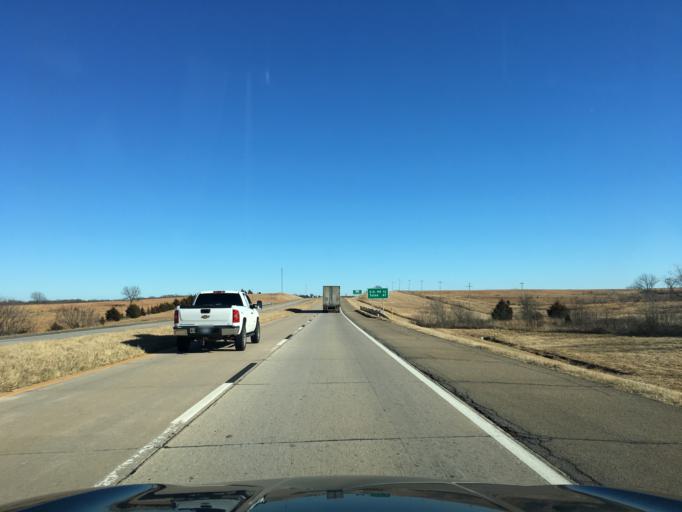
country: US
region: Oklahoma
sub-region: Pawnee County
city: Pawnee
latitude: 36.2248
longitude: -96.7672
